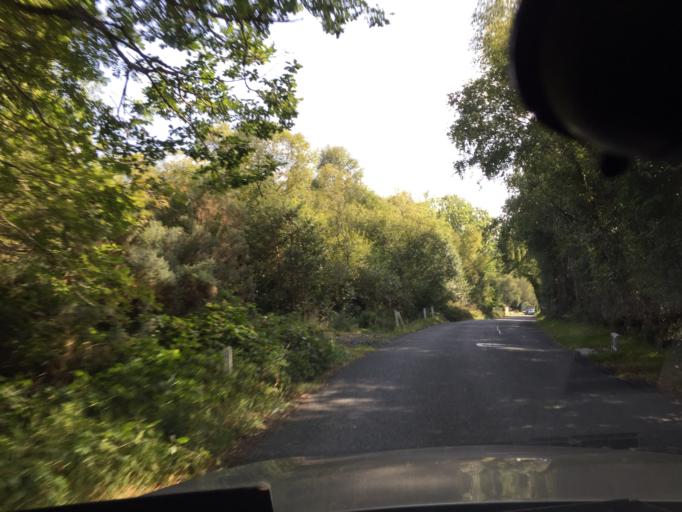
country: IE
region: Leinster
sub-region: Wicklow
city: Rathdrum
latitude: 53.0107
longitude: -6.2957
